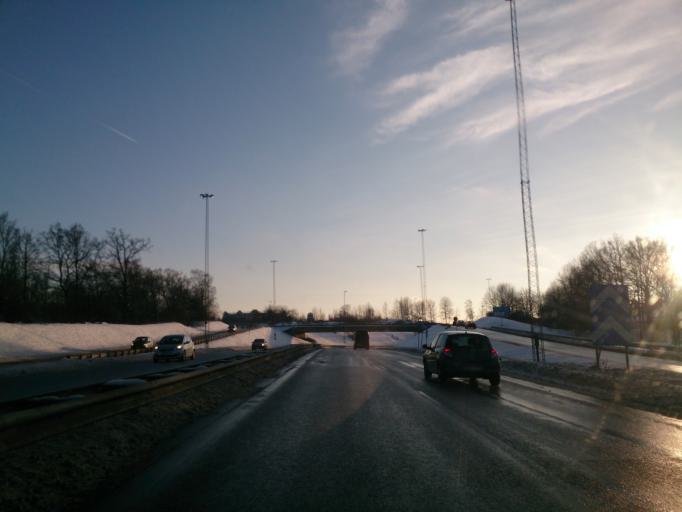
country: SE
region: OEstergoetland
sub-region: Norrkopings Kommun
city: Norrkoping
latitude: 58.5864
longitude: 16.1506
